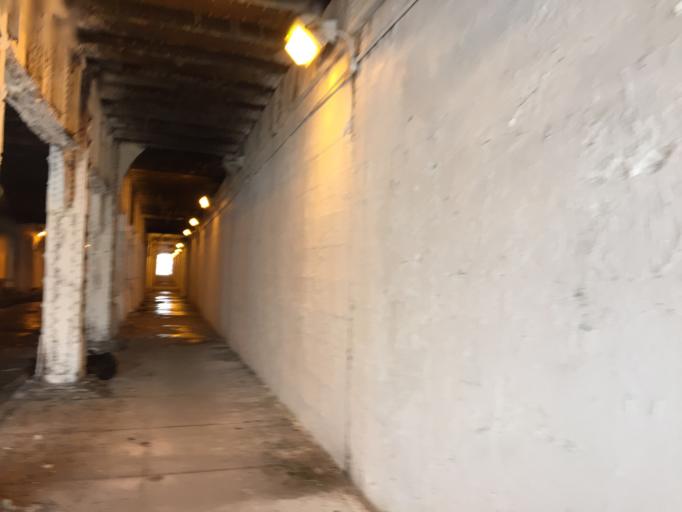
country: US
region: Illinois
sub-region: Cook County
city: Chicago
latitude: 41.8492
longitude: -87.6367
